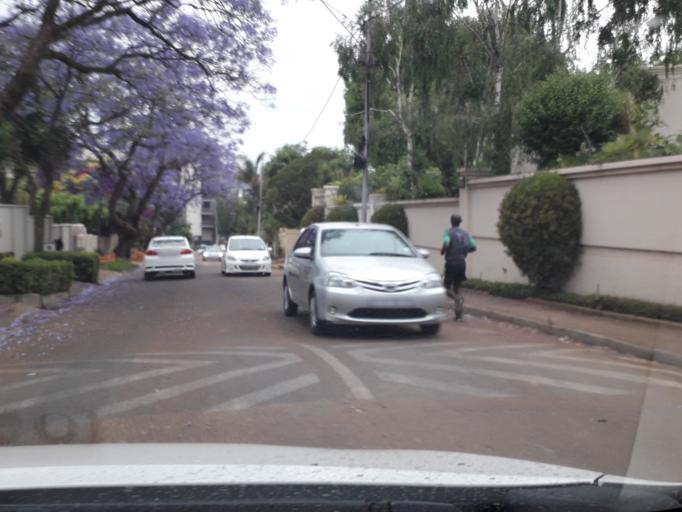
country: ZA
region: Gauteng
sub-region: City of Johannesburg Metropolitan Municipality
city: Johannesburg
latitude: -26.1332
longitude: 28.0649
